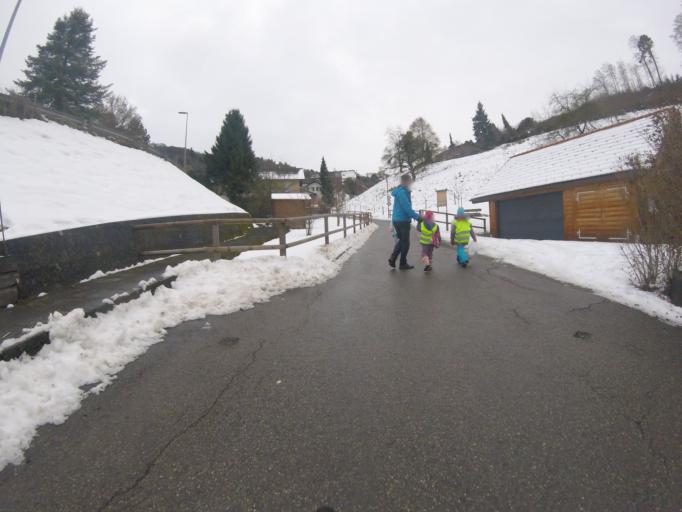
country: CH
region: Bern
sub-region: Bern-Mittelland District
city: Kehrsatz
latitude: 46.9089
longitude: 7.4681
